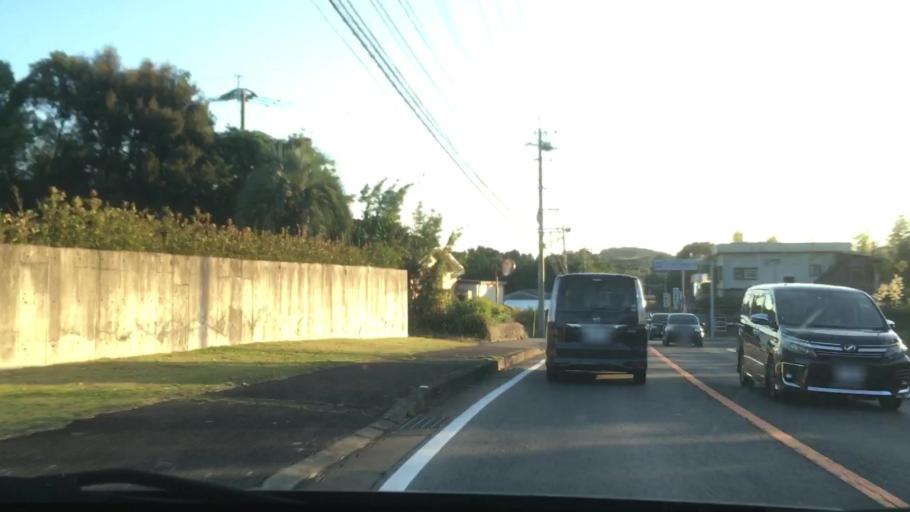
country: JP
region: Nagasaki
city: Sasebo
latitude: 33.0624
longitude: 129.7642
